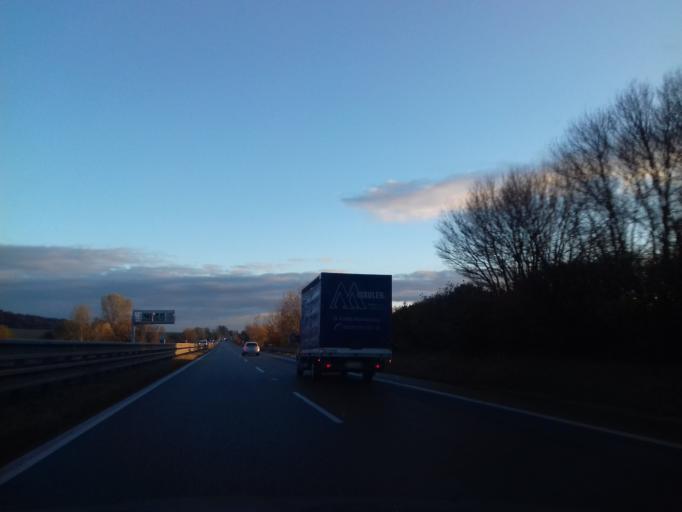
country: CZ
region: South Moravian
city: Pustimer
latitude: 49.3210
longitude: 17.0417
